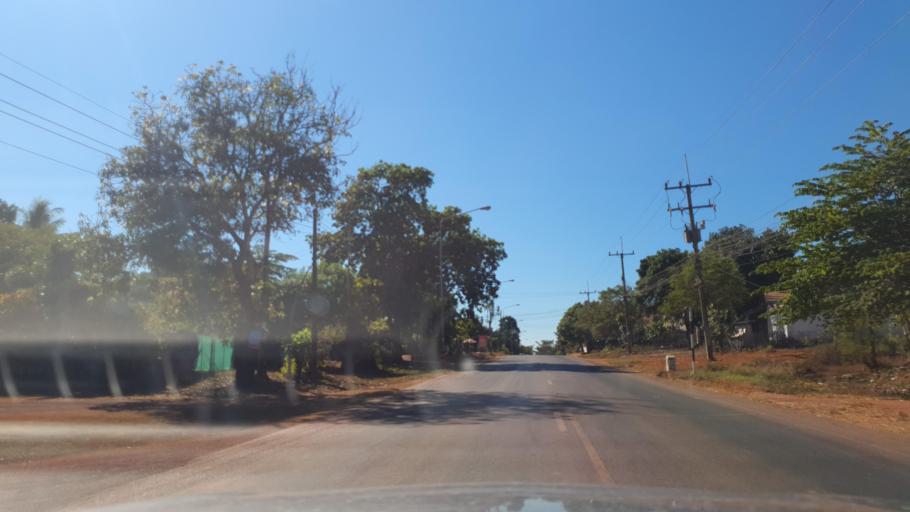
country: TH
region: Nakhon Phanom
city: Si Songkhram
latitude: 17.7587
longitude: 104.2865
